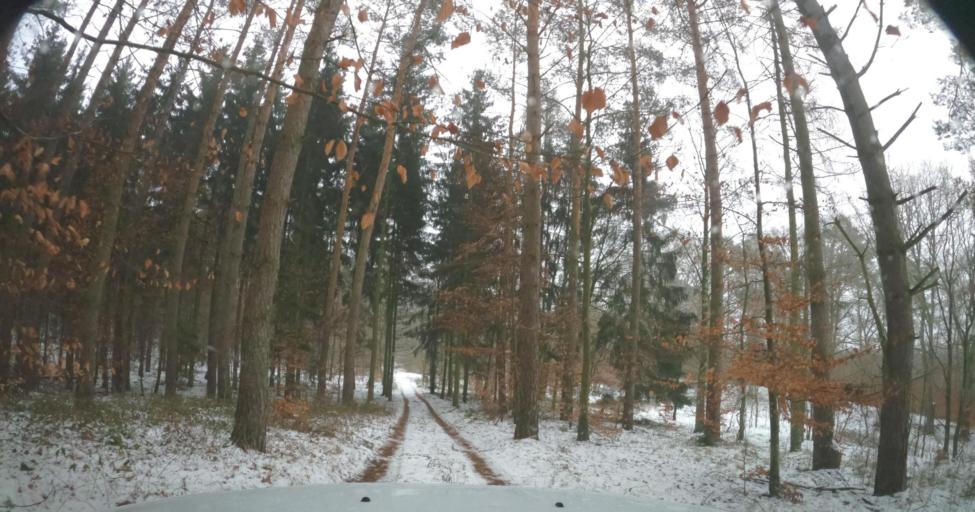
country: PL
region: West Pomeranian Voivodeship
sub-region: Powiat kamienski
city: Golczewo
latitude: 53.8692
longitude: 15.0438
